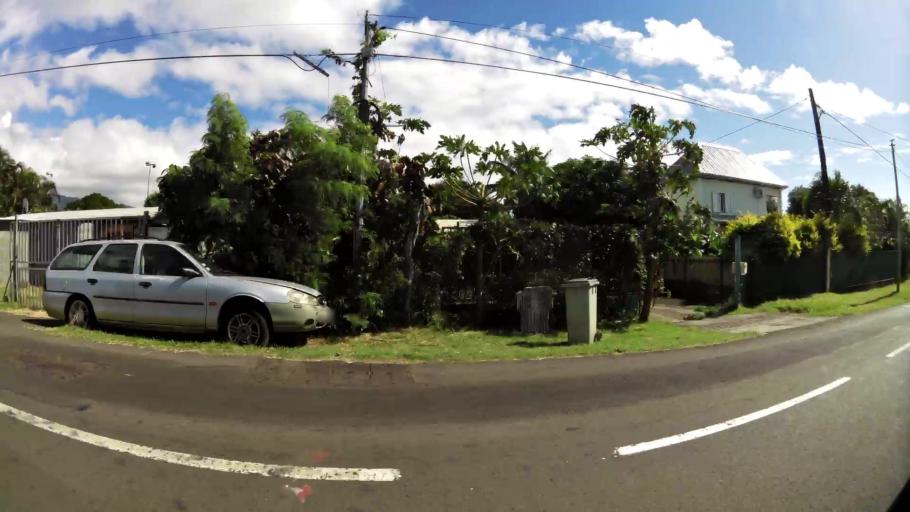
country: RE
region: Reunion
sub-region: Reunion
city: Sainte-Marie
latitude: -20.8936
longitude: 55.5094
